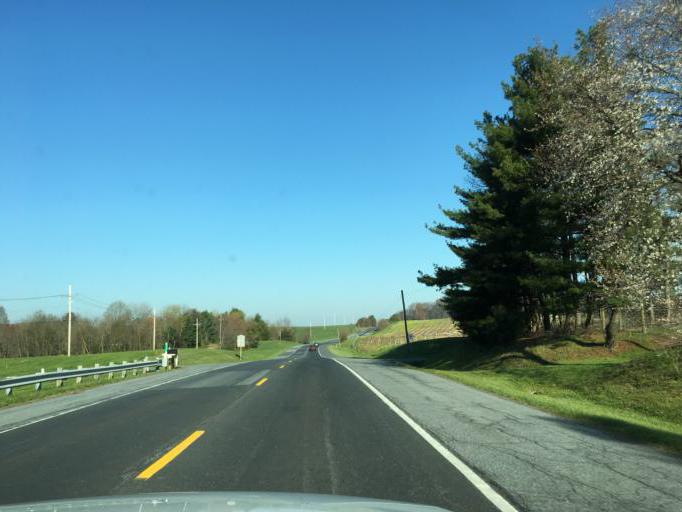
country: US
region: Maryland
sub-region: Frederick County
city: Linganore
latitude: 39.4651
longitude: -77.1368
